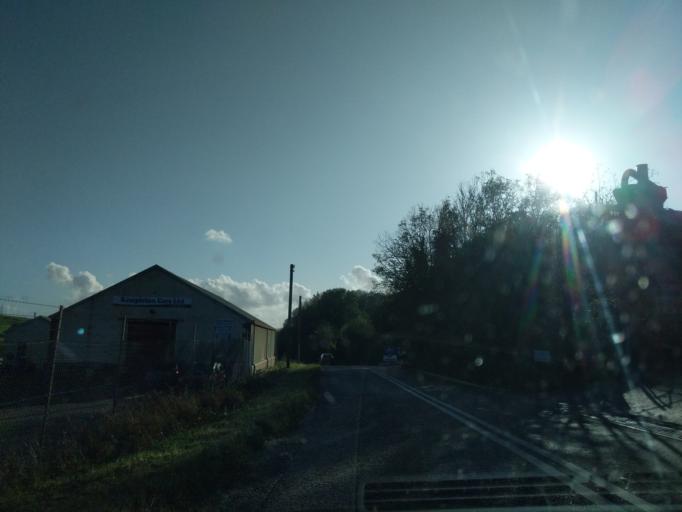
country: GB
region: Scotland
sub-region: Dumfries and Galloway
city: Kirkcudbright
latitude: 54.8678
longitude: -4.0274
